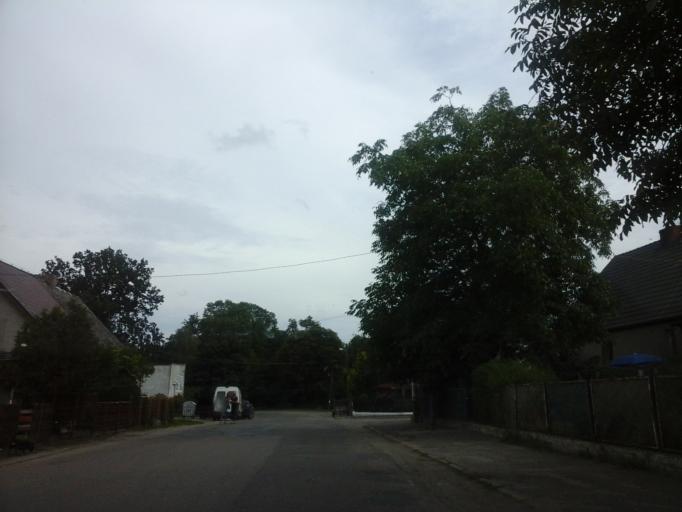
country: PL
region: West Pomeranian Voivodeship
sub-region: Powiat stargardzki
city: Marianowo
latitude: 53.3398
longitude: 15.1916
